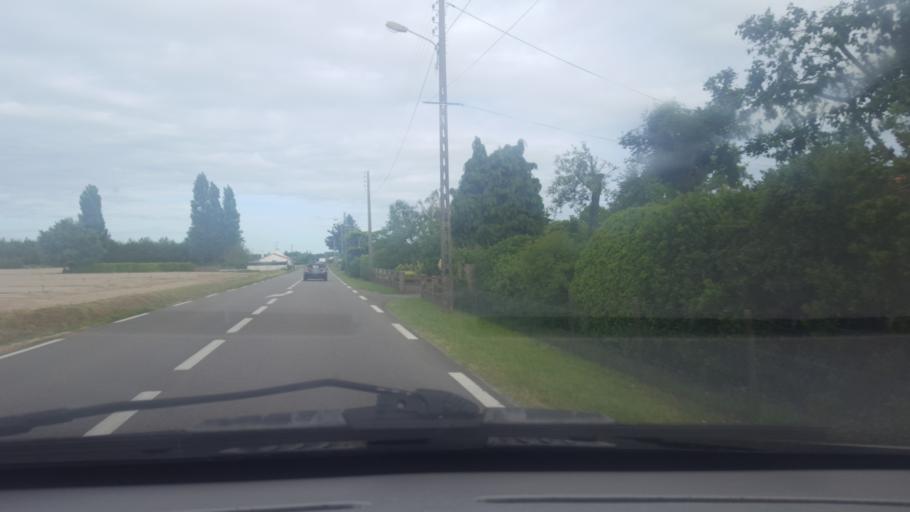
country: FR
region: Pays de la Loire
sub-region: Departement de la Loire-Atlantique
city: Bourgneuf-en-Retz
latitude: 47.0282
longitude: -1.8930
